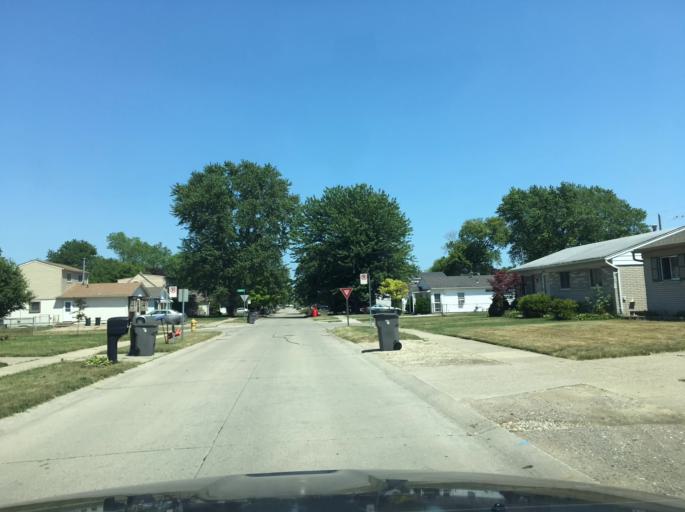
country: US
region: Michigan
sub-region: Macomb County
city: Fraser
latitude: 42.5427
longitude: -82.9140
